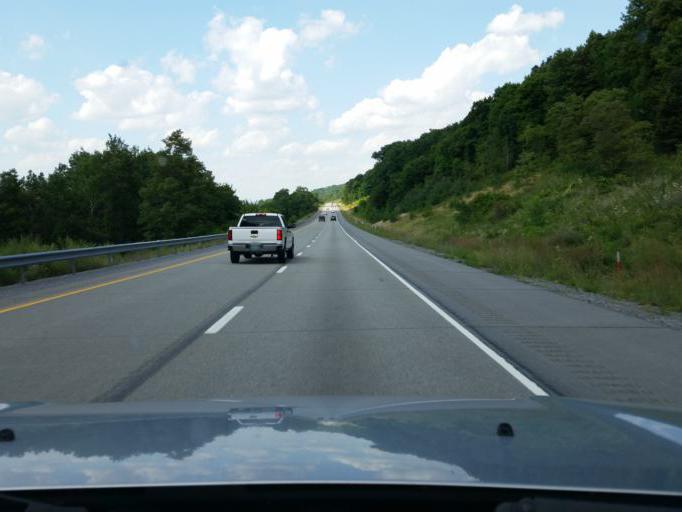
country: US
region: Pennsylvania
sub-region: Blair County
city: Claysburg
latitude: 40.3217
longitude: -78.4356
